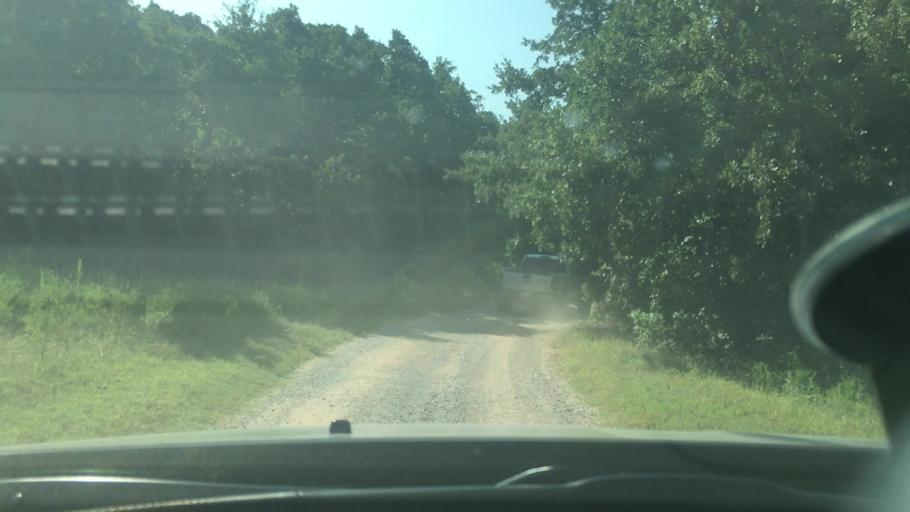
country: US
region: Oklahoma
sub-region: Garvin County
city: Lindsay
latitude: 34.7660
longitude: -97.6162
